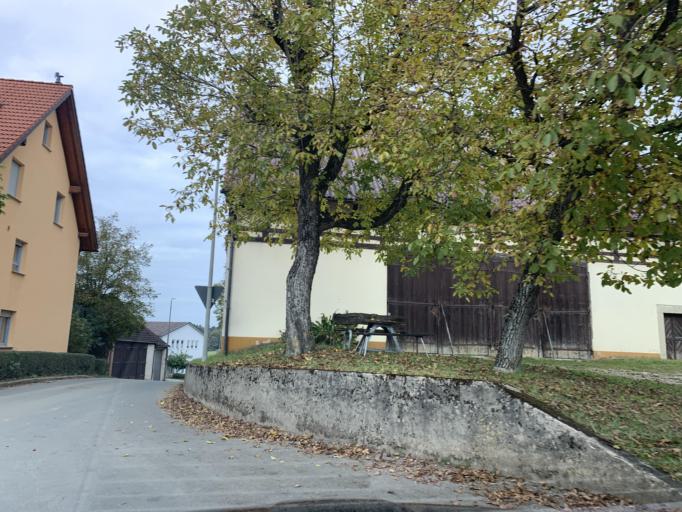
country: DE
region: Bavaria
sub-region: Upper Franconia
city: Unterleinleiter
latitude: 49.8432
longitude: 11.2454
